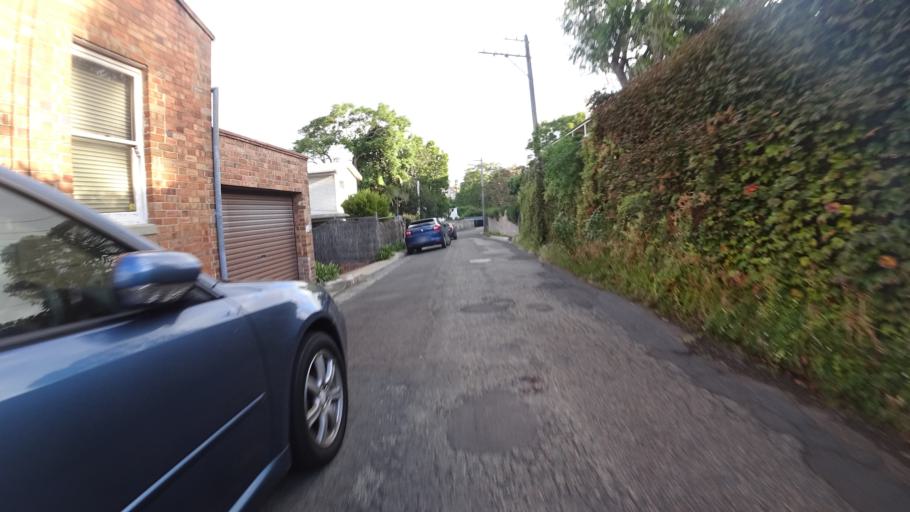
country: AU
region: New South Wales
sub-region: Lane Cove
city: Longueville
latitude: -33.8356
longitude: 151.1579
